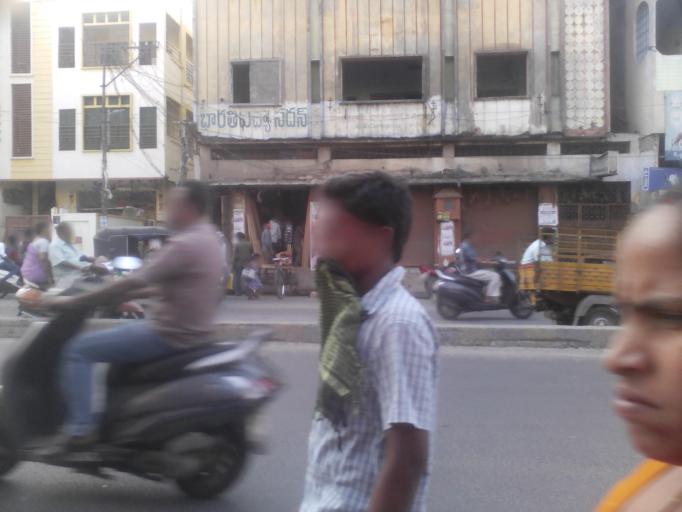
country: IN
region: Andhra Pradesh
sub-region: Krishna
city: Vijayawada
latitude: 16.5288
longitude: 80.6114
